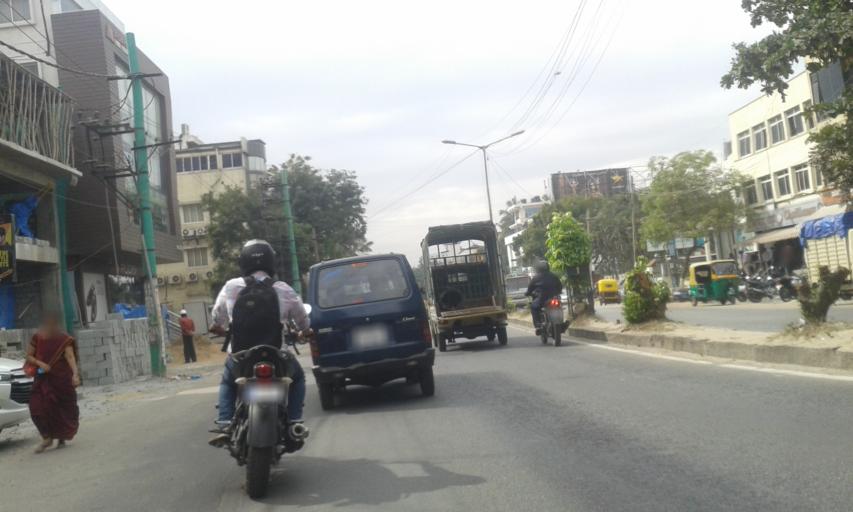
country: IN
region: Karnataka
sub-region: Bangalore Urban
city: Bangalore
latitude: 12.9061
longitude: 77.5966
